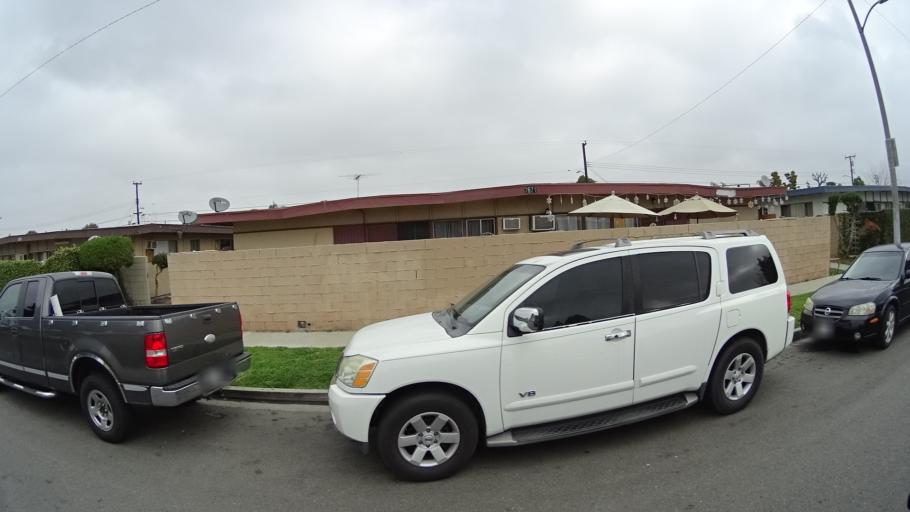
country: US
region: California
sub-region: Orange County
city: Buena Park
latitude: 33.8370
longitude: -117.9996
